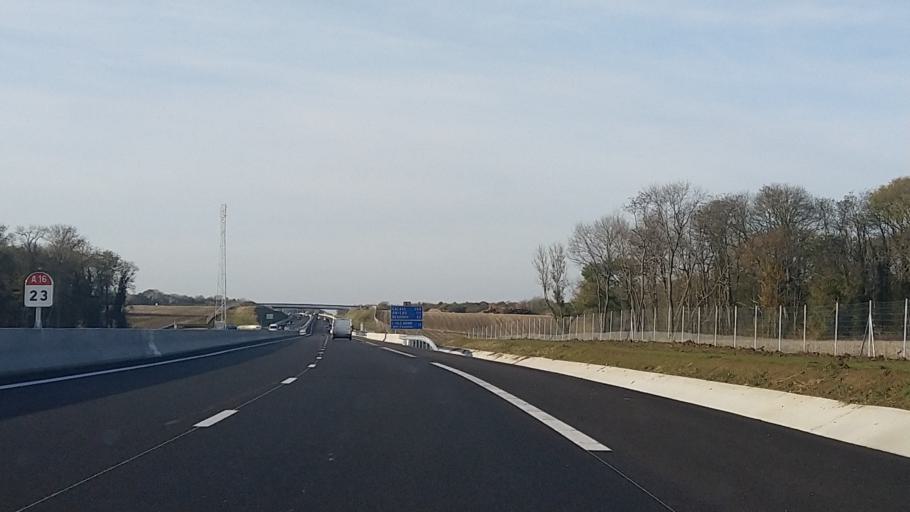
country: FR
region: Ile-de-France
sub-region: Departement du Val-d'Oise
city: Montsoult
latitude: 49.0815
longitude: 2.3278
